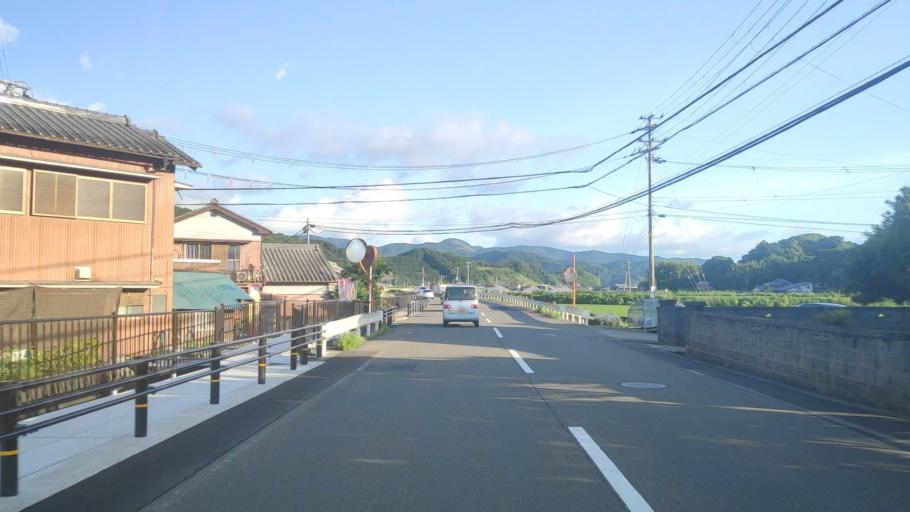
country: JP
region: Wakayama
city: Tanabe
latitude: 33.7192
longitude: 135.4458
